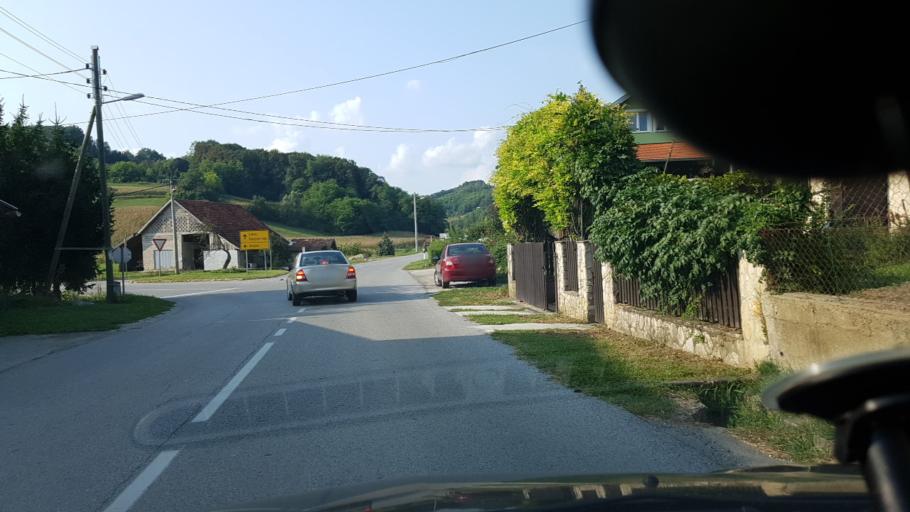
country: SI
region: Bistrica ob Sotli
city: Bistrica ob Sotli
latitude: 46.0357
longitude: 15.7733
